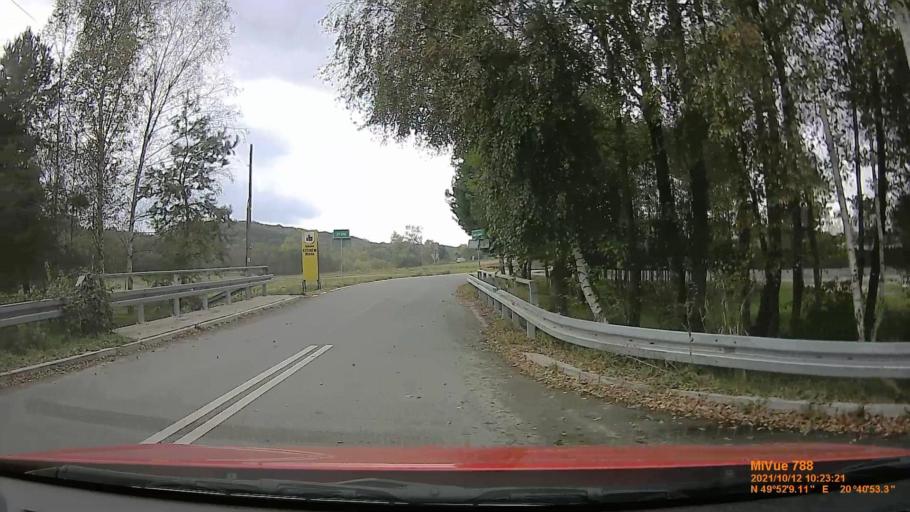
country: PL
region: Lesser Poland Voivodeship
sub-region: Powiat brzeski
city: Zlota
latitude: 49.8692
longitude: 20.6814
